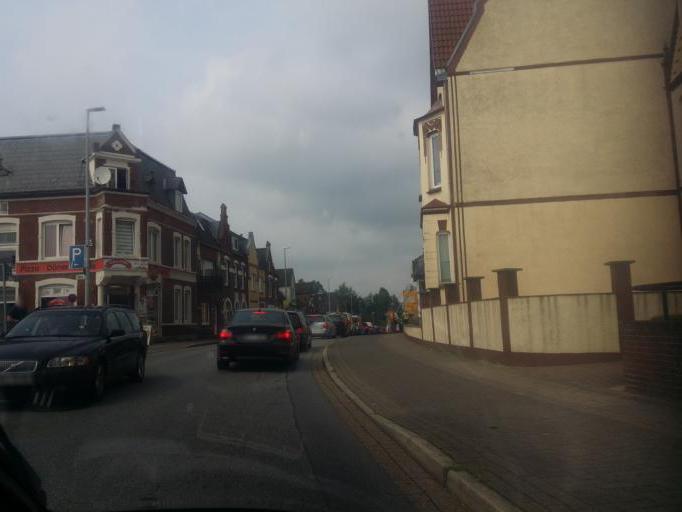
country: DE
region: Schleswig-Holstein
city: Husum
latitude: 54.4705
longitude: 9.0516
